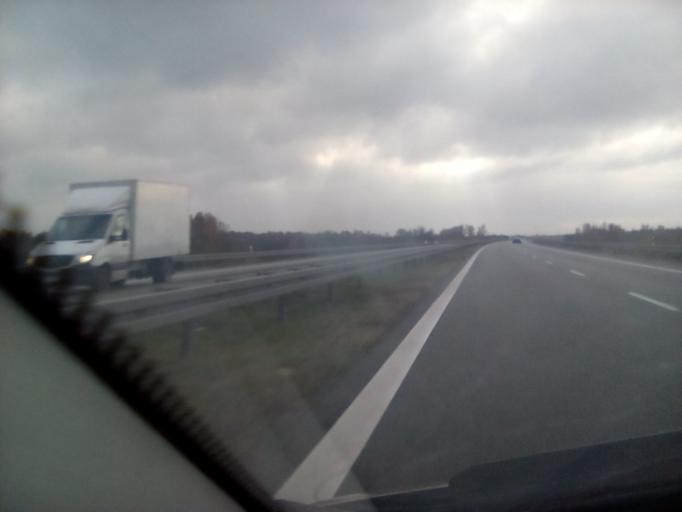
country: PL
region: Masovian Voivodeship
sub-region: Powiat bialobrzeski
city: Bialobrzegi
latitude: 51.6592
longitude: 20.9629
